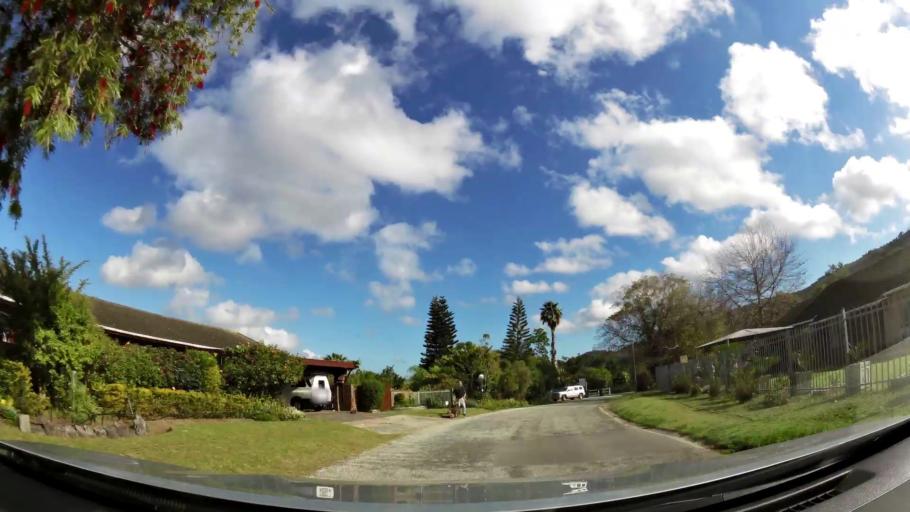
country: ZA
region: Western Cape
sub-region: Eden District Municipality
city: Knysna
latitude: -34.0428
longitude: 23.0712
